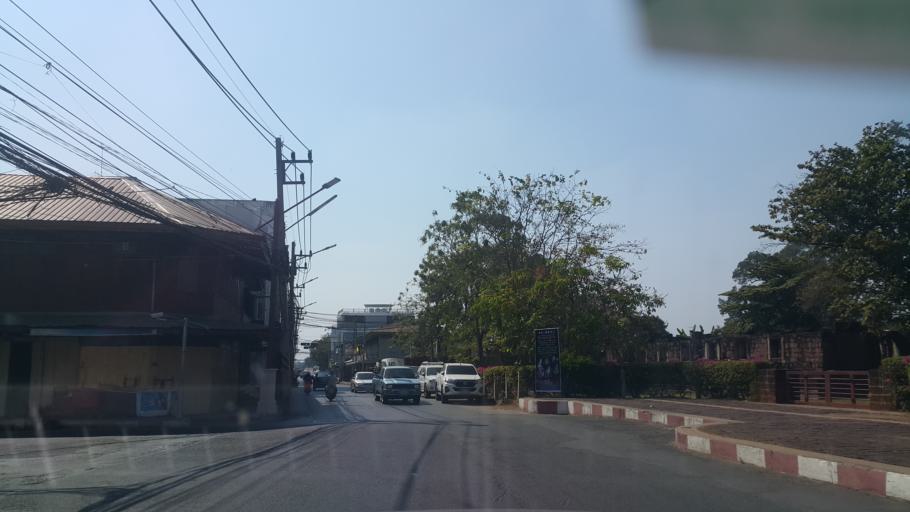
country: TH
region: Nakhon Ratchasima
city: Phimai
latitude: 15.2189
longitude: 102.4949
